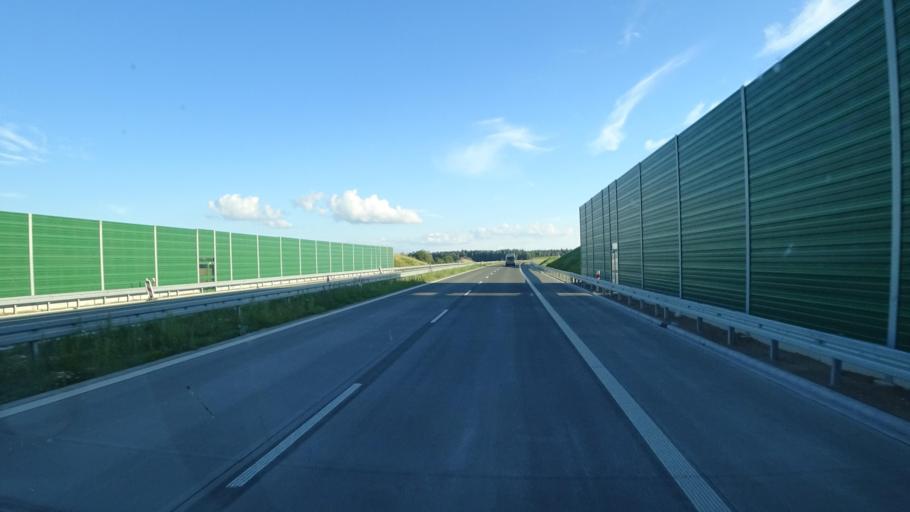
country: PL
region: Podlasie
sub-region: Powiat suwalski
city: Raczki
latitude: 53.9396
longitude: 22.7626
